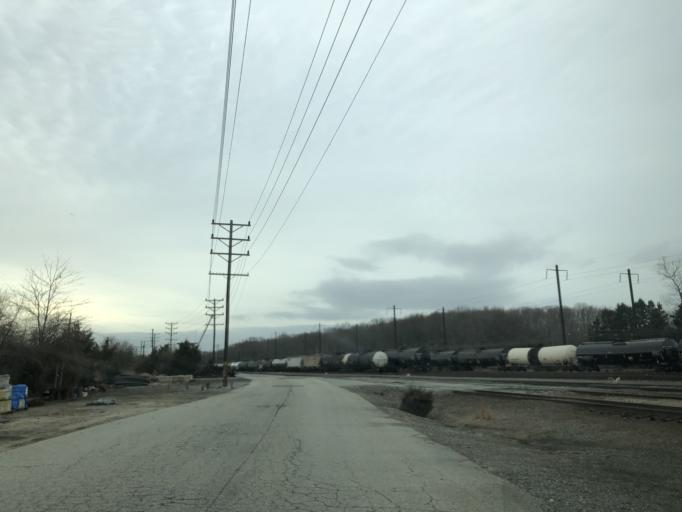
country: US
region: Delaware
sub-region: New Castle County
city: Newark
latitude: 39.6657
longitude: -75.7644
